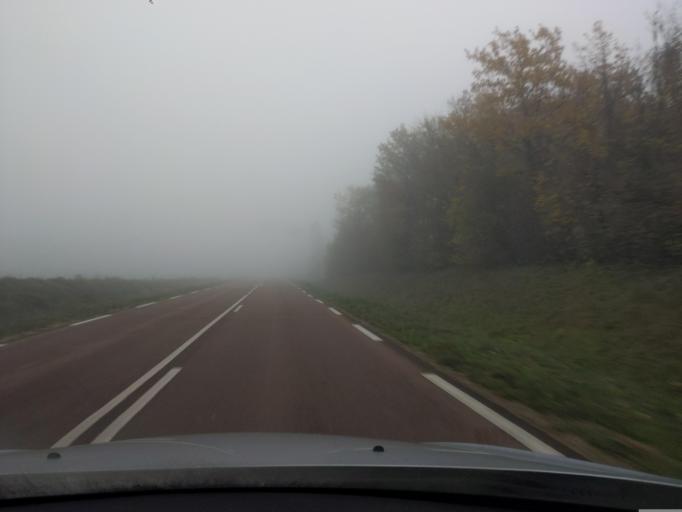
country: FR
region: Champagne-Ardenne
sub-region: Departement de la Haute-Marne
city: Langres
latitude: 47.8172
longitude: 5.2974
